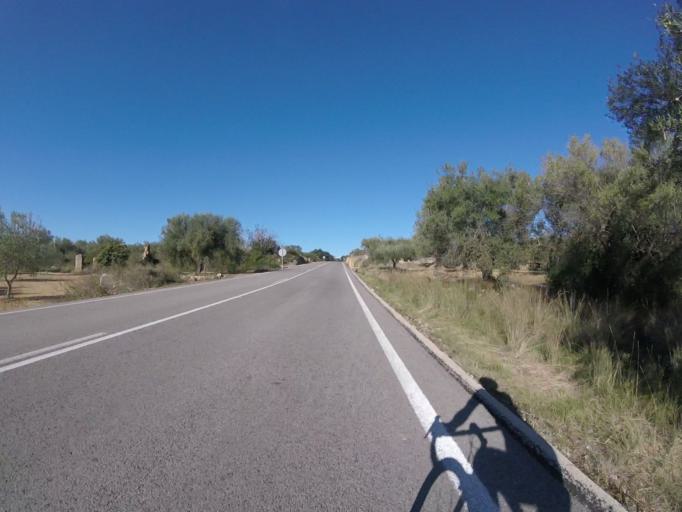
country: ES
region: Valencia
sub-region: Provincia de Castello
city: Cervera del Maestre
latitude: 40.4730
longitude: 0.2361
